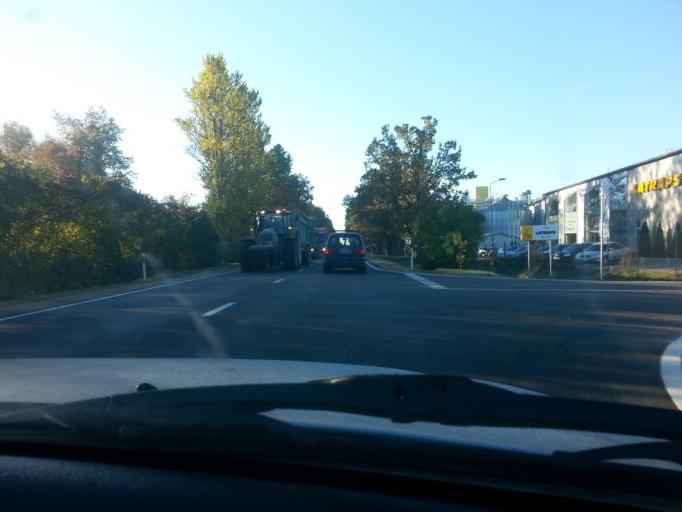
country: LT
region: Siauliu apskritis
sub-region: Joniskis
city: Joniskis
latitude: 56.4219
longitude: 23.6846
